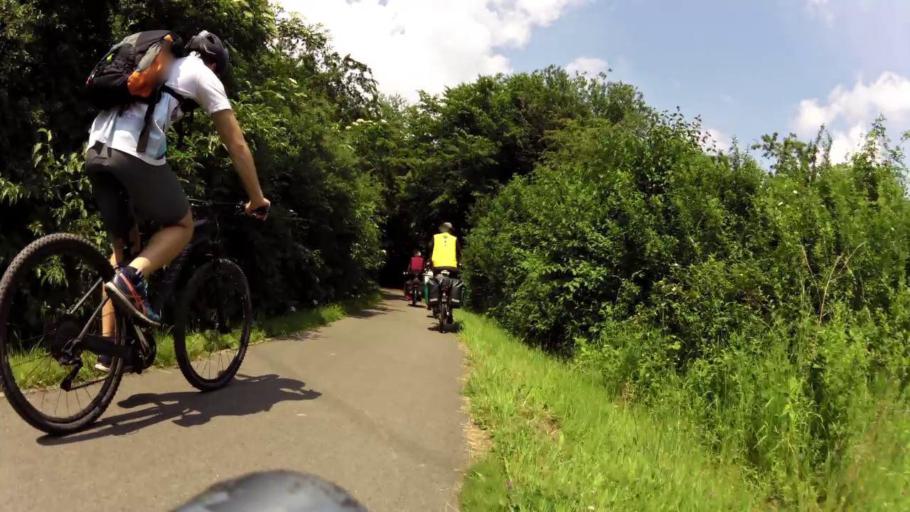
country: PL
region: Kujawsko-Pomorskie
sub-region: Powiat bydgoski
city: Koronowo
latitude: 53.2955
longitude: 17.9484
